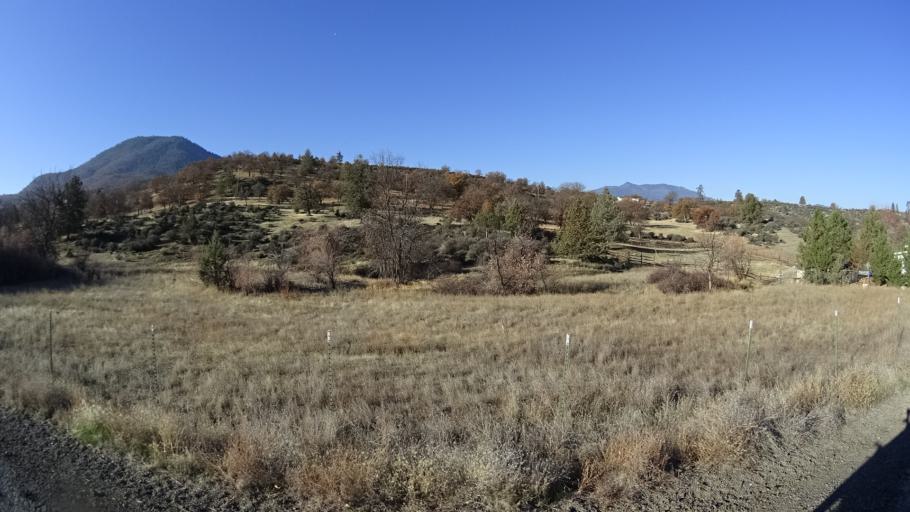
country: US
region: California
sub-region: Siskiyou County
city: Montague
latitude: 41.8932
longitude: -122.4931
